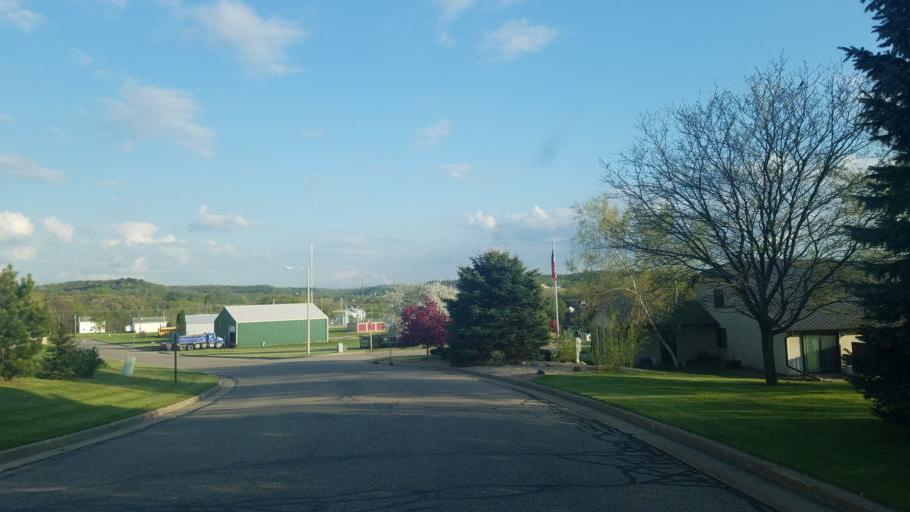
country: US
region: Wisconsin
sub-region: Vernon County
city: Hillsboro
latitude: 43.6593
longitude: -90.3375
